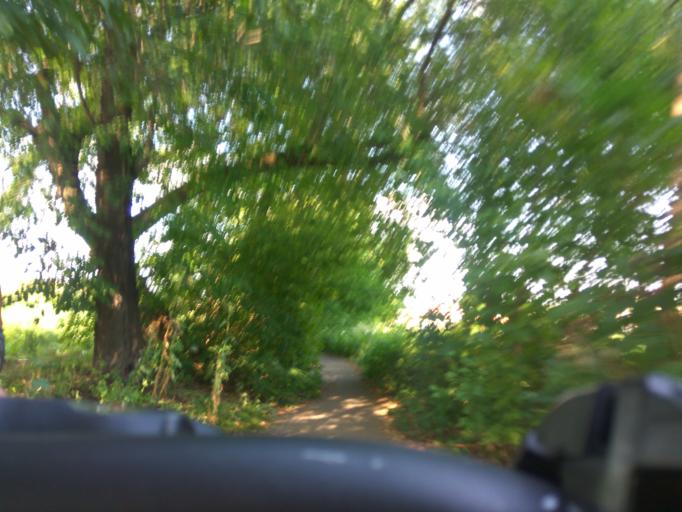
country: RU
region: Moscow
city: Orekhovo-Borisovo Severnoye
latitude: 55.6176
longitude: 37.6702
